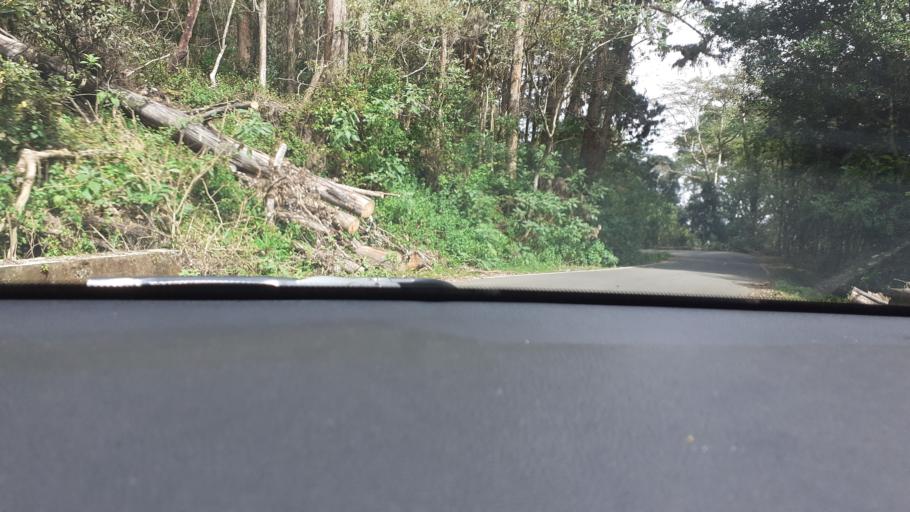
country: IN
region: Tamil Nadu
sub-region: Dindigul
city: Kodaikanal
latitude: 10.2375
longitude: 77.4222
